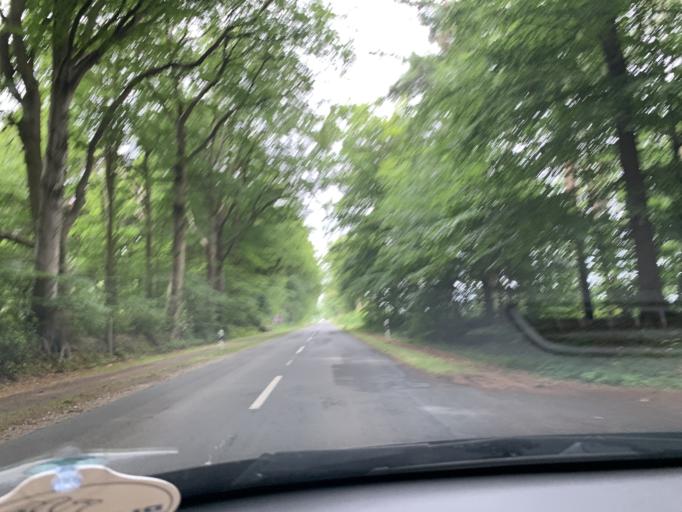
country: DE
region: Lower Saxony
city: Bockhorn
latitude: 53.3488
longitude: 8.0494
